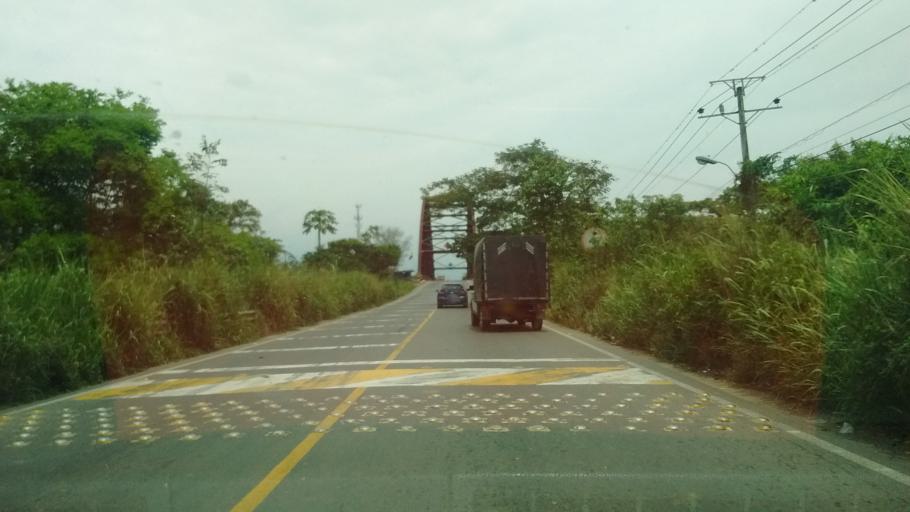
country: CO
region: Valle del Cauca
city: Jamundi
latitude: 3.3002
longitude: -76.4756
